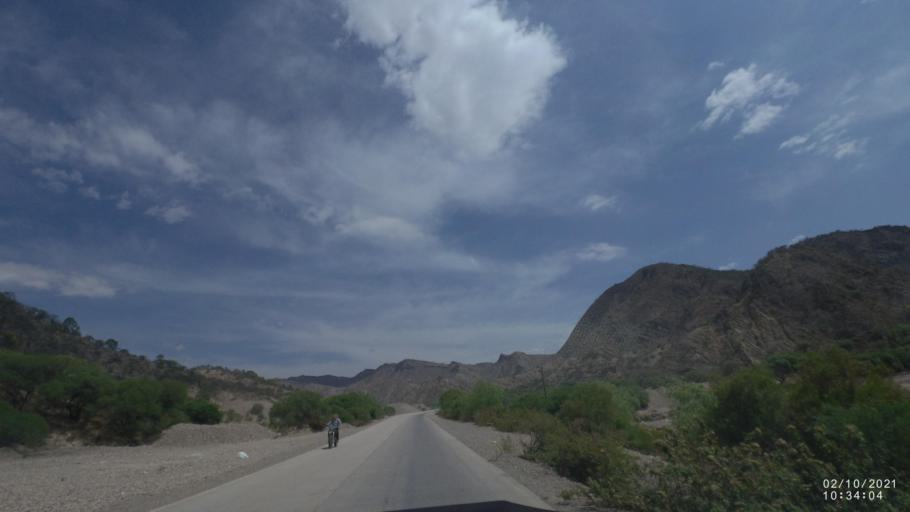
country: BO
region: Cochabamba
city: Capinota
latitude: -17.6763
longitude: -66.2511
